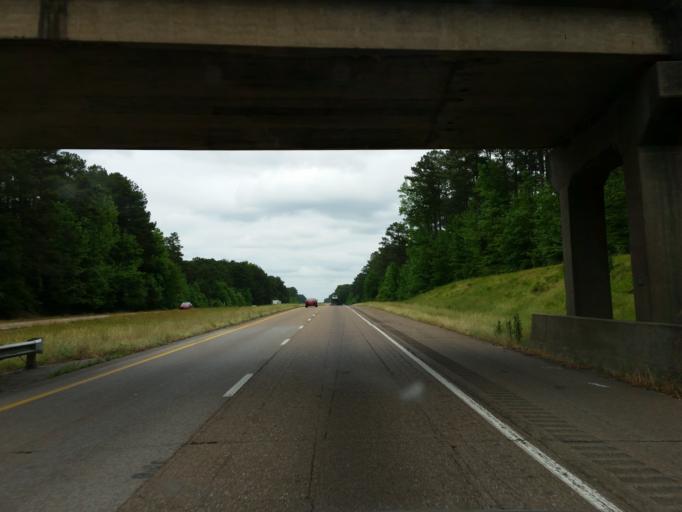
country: US
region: Mississippi
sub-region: Lauderdale County
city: Marion
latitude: 32.3909
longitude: -88.5959
